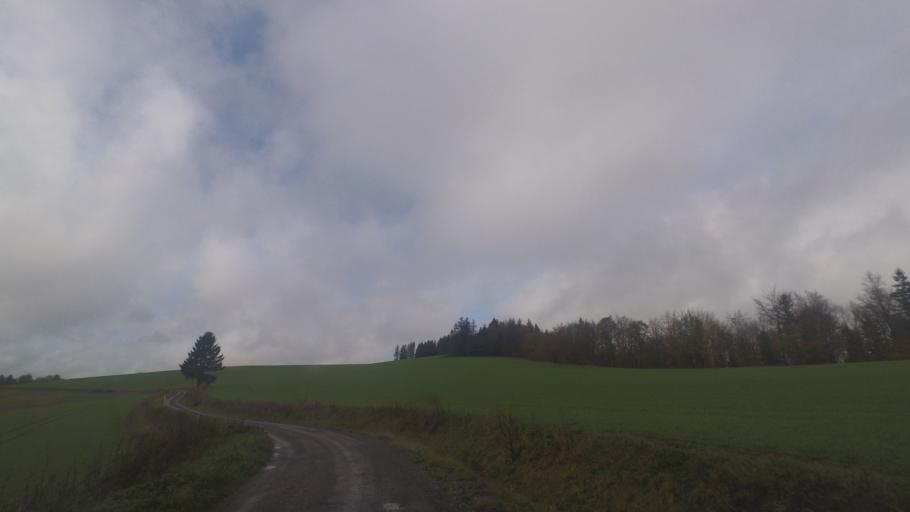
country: DE
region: Thuringia
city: Eisfeld
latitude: 50.4848
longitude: 10.8639
